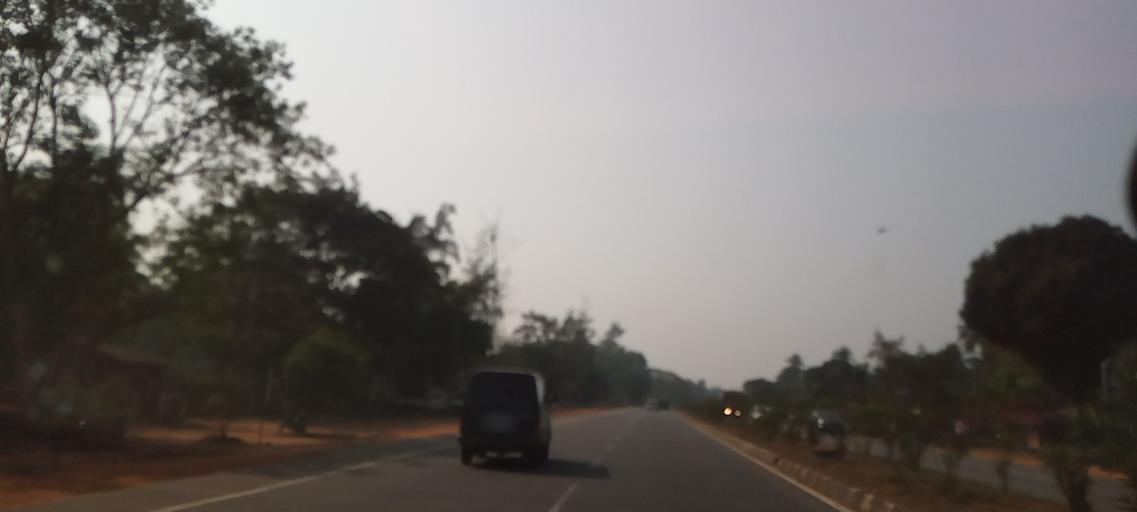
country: IN
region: Karnataka
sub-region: Udupi
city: Coondapoor
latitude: 13.5205
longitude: 74.7060
